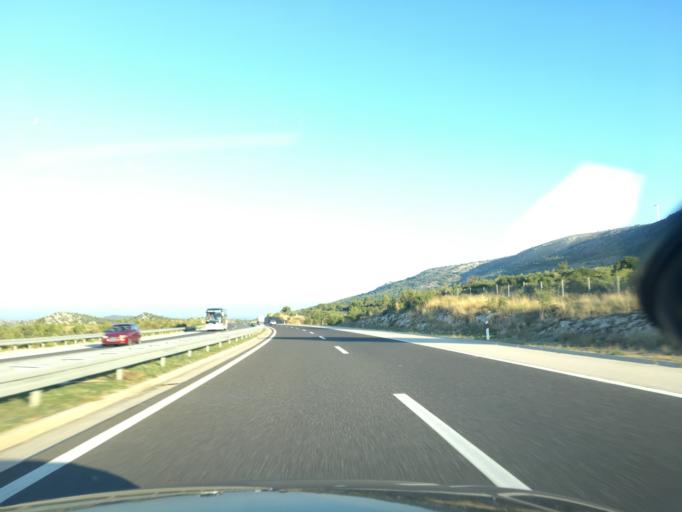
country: HR
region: Sibensko-Kniniska
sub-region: Grad Sibenik
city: Sibenik
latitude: 43.7425
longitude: 15.9642
